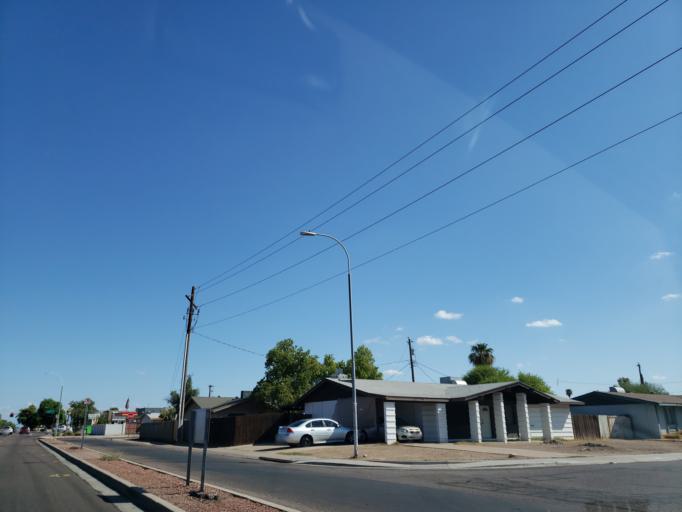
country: US
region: Arizona
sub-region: Maricopa County
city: Tolleson
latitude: 33.4924
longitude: -112.2377
